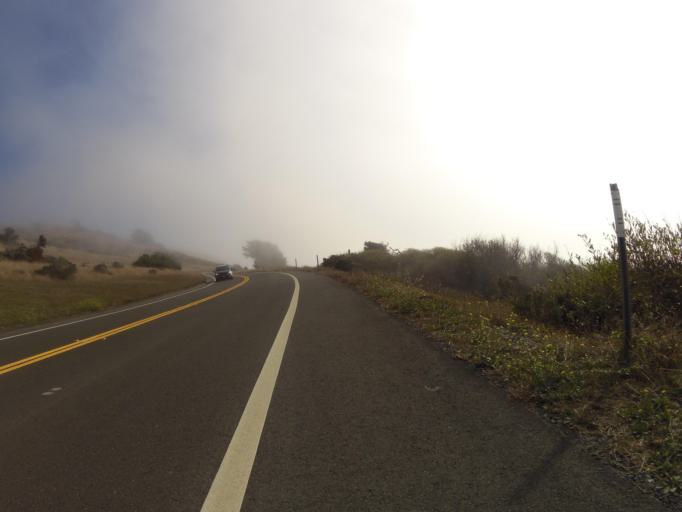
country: US
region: California
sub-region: Sonoma County
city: Sea Ranch
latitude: 38.8622
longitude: -123.6568
